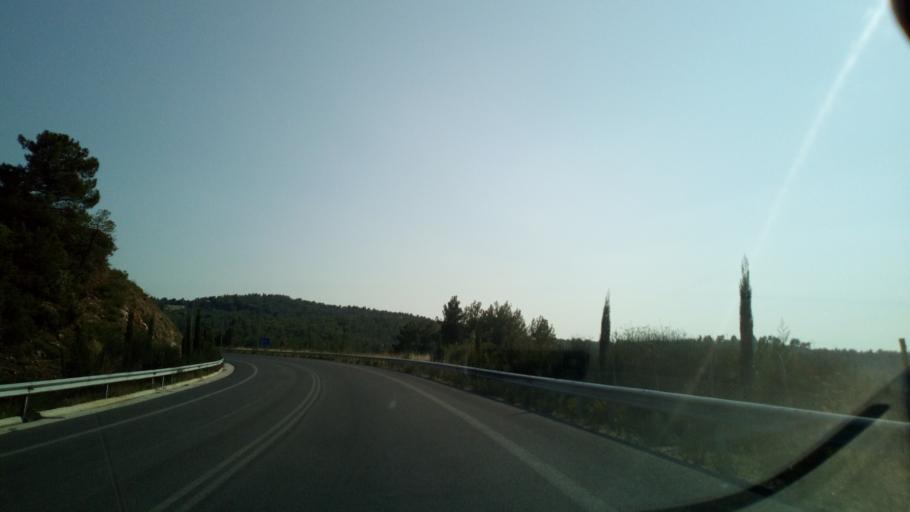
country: GR
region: Central Macedonia
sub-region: Nomos Chalkidikis
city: Polygyros
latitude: 40.3679
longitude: 23.4406
